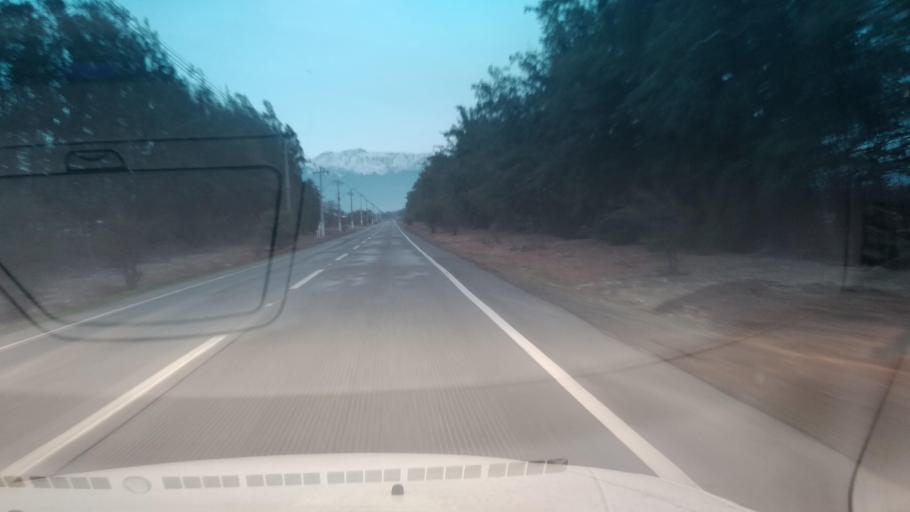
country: CL
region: Santiago Metropolitan
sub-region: Provincia de Chacabuco
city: Chicureo Abajo
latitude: -33.0944
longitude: -70.7008
